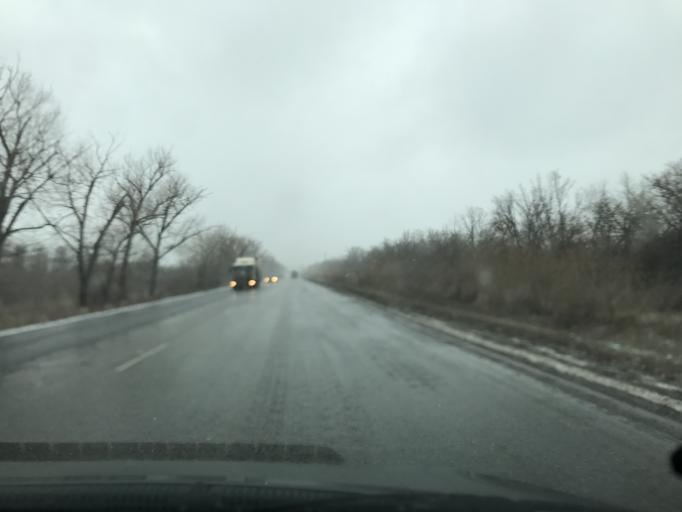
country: RU
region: Rostov
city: Bataysk
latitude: 47.0748
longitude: 39.7873
